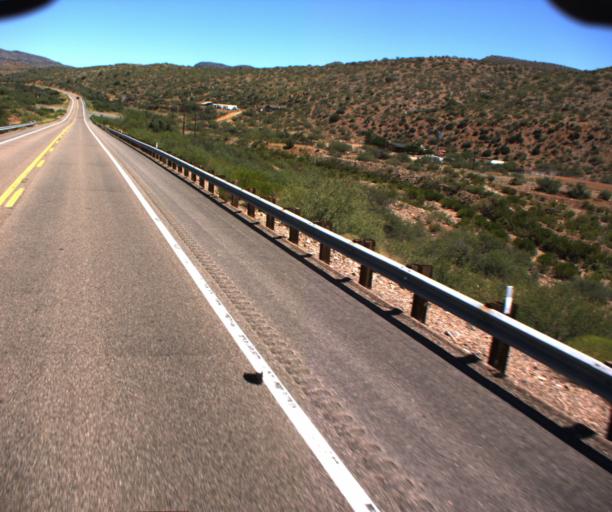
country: US
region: Arizona
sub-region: Gila County
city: Globe
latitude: 33.4442
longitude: -110.7222
